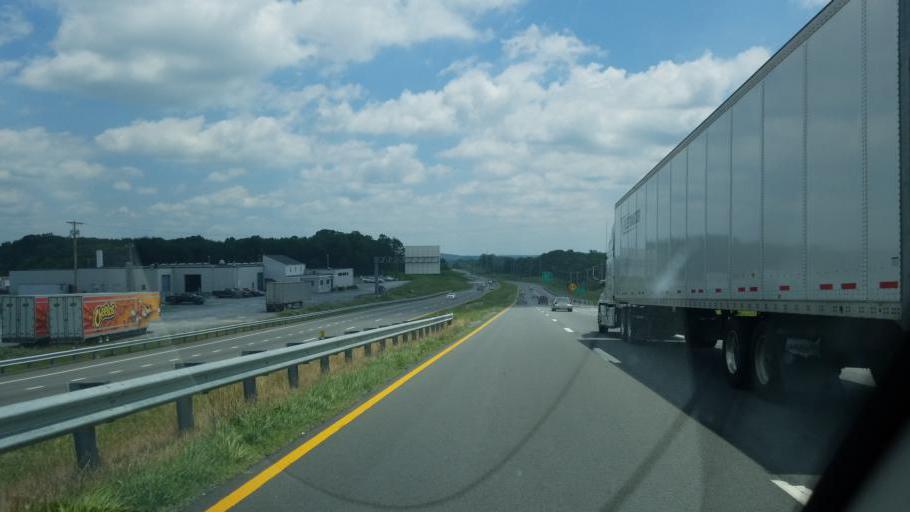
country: US
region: Virginia
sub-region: City of Lynchburg
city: Lynchburg
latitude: 37.3797
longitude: -79.1236
